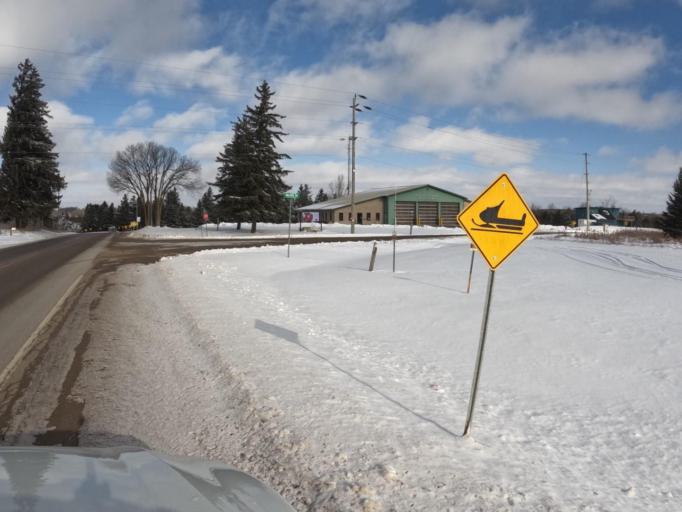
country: CA
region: Ontario
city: Orangeville
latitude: 43.8873
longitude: -80.3128
